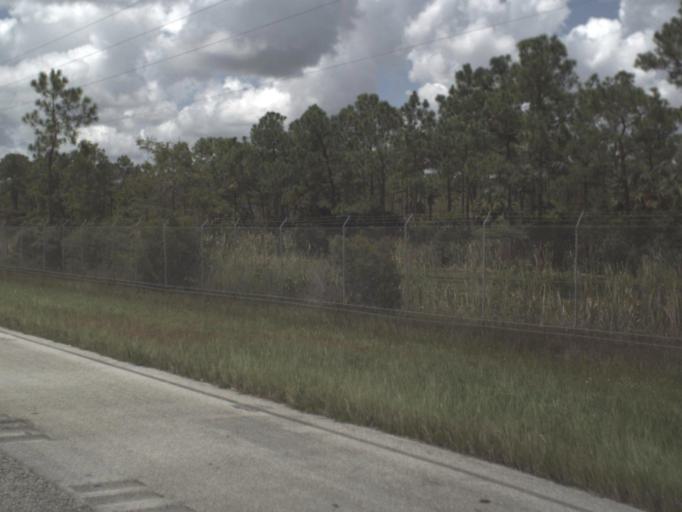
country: US
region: Florida
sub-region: Collier County
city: Immokalee
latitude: 26.1705
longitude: -80.9912
